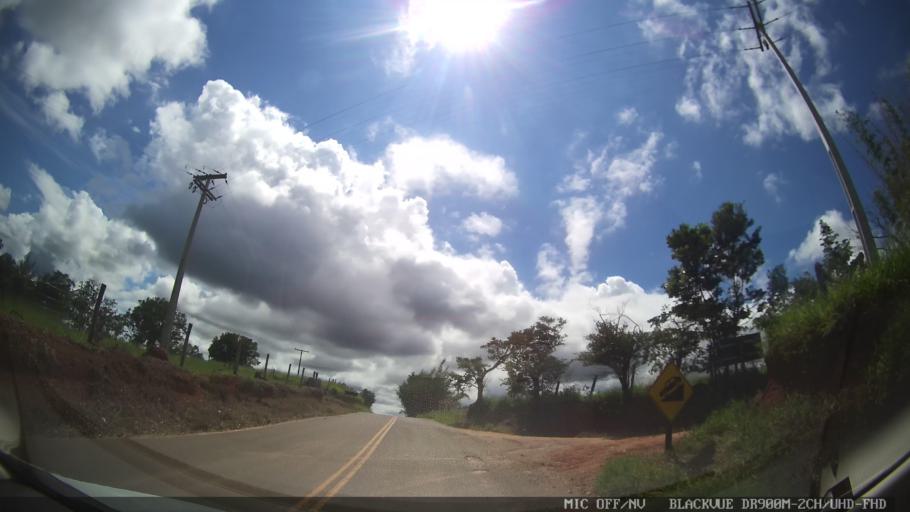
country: BR
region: Sao Paulo
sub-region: Braganca Paulista
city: Braganca Paulista
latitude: -22.8643
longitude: -46.6678
